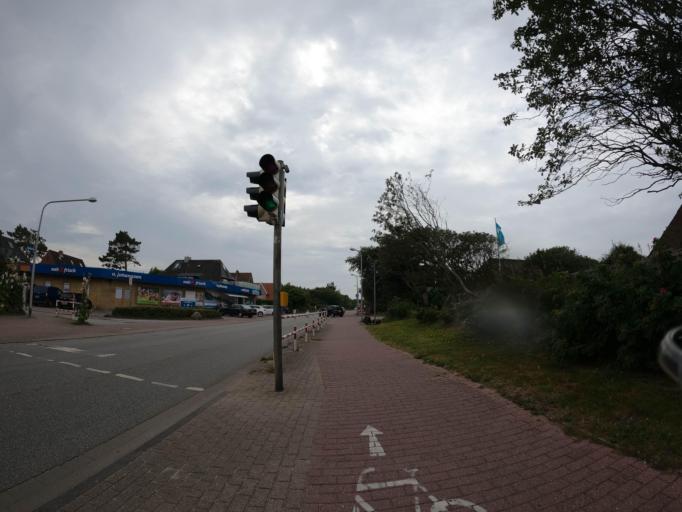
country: DE
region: Schleswig-Holstein
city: Westerland
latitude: 54.9253
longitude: 8.3156
